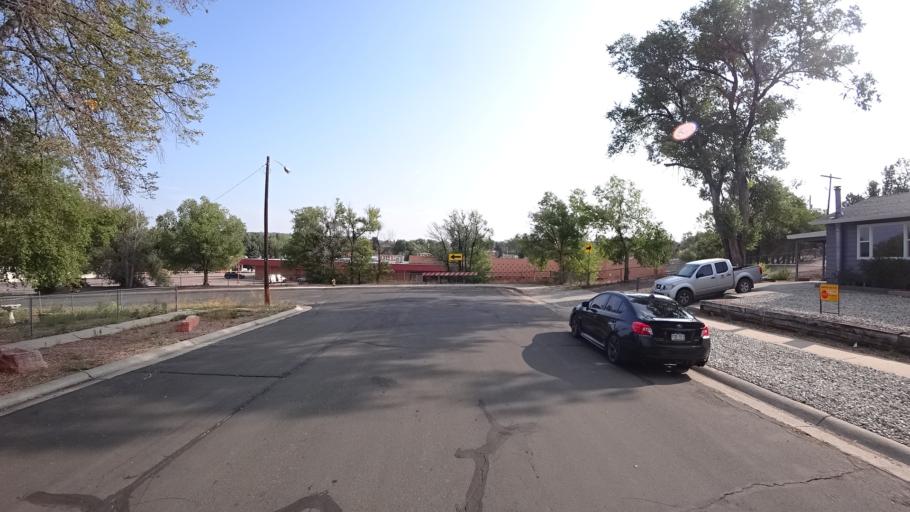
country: US
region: Colorado
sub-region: El Paso County
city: Colorado Springs
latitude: 38.8530
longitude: -104.7787
